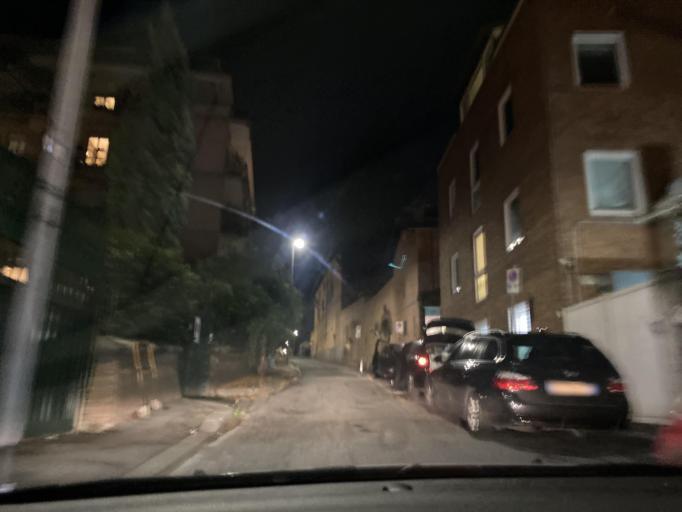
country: VA
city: Vatican City
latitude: 41.9202
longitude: 12.4802
